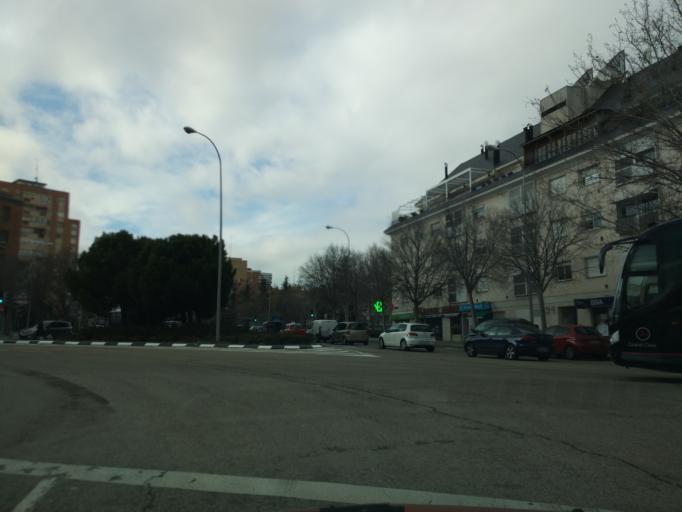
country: ES
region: Madrid
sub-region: Provincia de Madrid
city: Hortaleza
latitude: 40.4697
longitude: -3.6423
